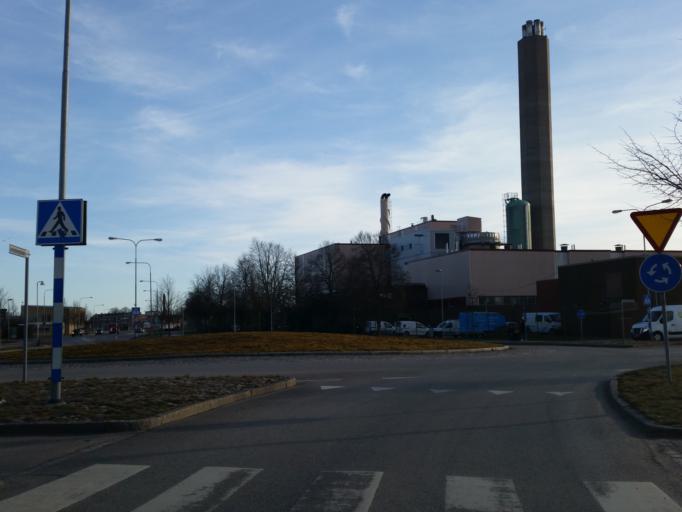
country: SE
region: Kalmar
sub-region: Kalmar Kommun
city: Kalmar
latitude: 56.6695
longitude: 16.3420
